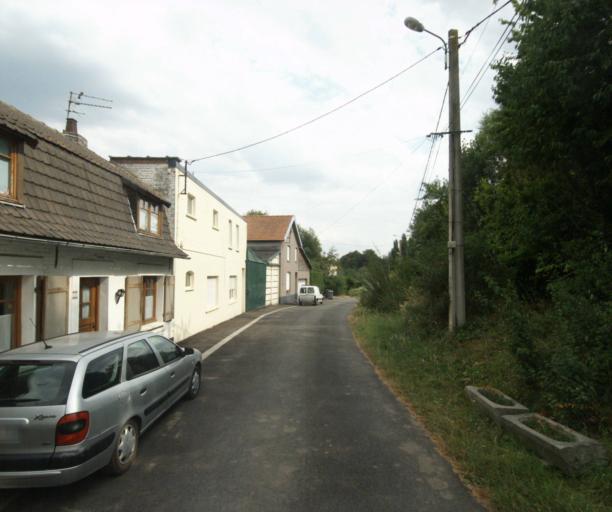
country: FR
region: Nord-Pas-de-Calais
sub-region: Departement du Nord
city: Neuville-en-Ferrain
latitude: 50.7653
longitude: 3.1637
